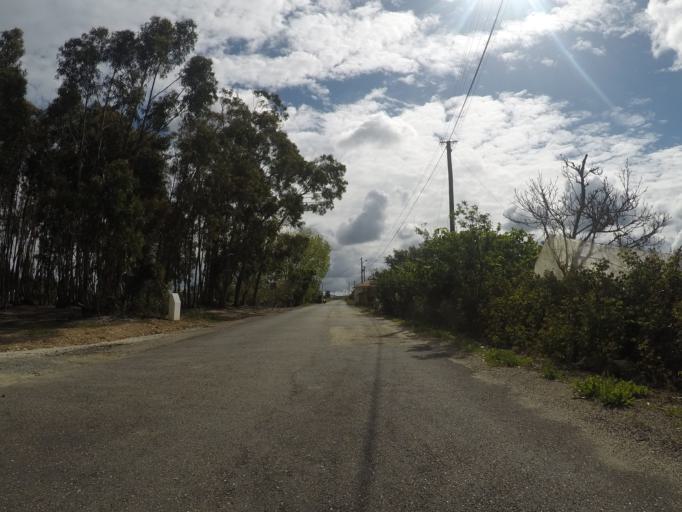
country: PT
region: Beja
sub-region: Odemira
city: Sao Teotonio
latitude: 37.4806
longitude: -8.7714
